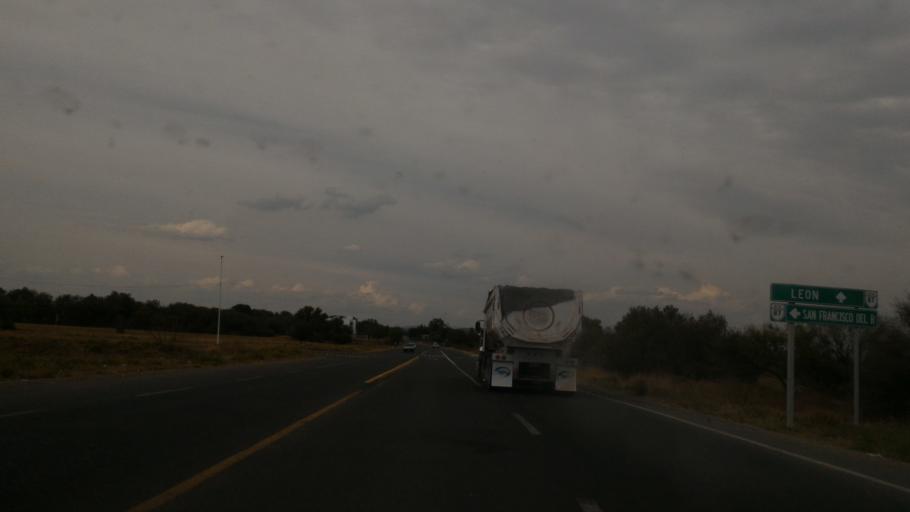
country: MX
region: Guanajuato
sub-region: San Francisco del Rincon
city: Fraccionamiento la Mezquitera
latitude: 21.0106
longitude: -101.8289
